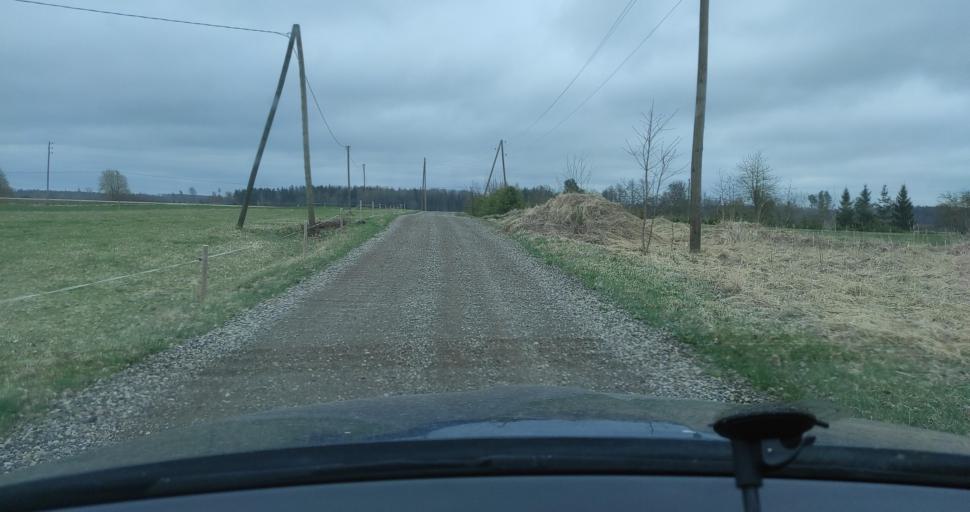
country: LV
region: Saldus Rajons
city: Saldus
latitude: 56.6303
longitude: 22.4273
